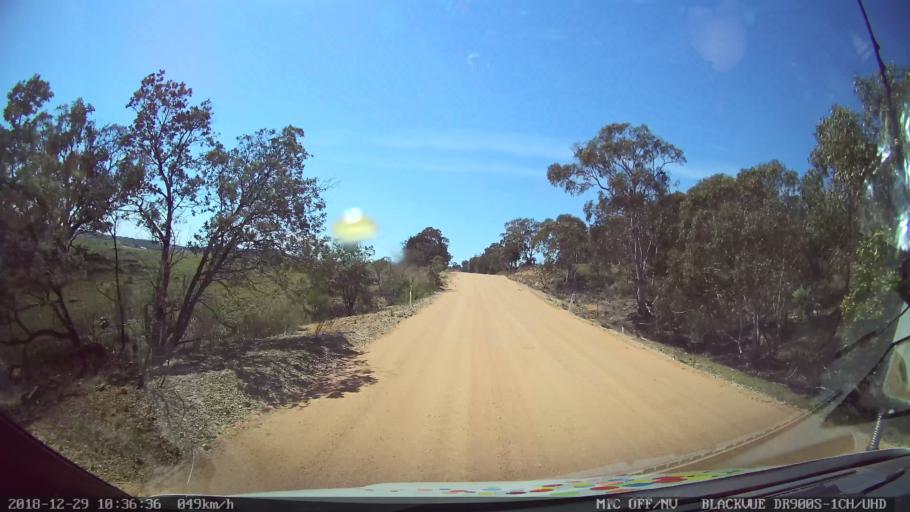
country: AU
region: New South Wales
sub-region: Yass Valley
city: Gundaroo
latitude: -34.9947
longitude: 149.4919
